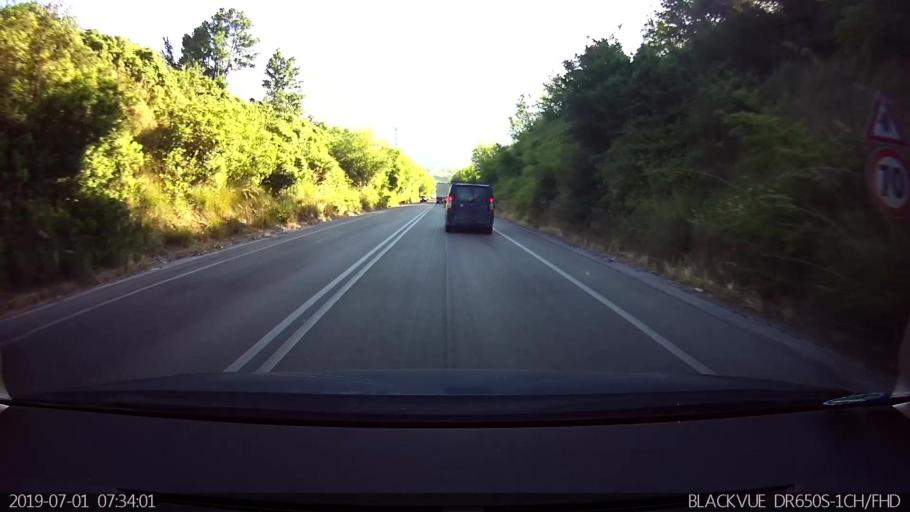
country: IT
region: Latium
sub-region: Provincia di Latina
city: Prossedi
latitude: 41.5123
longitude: 13.2684
